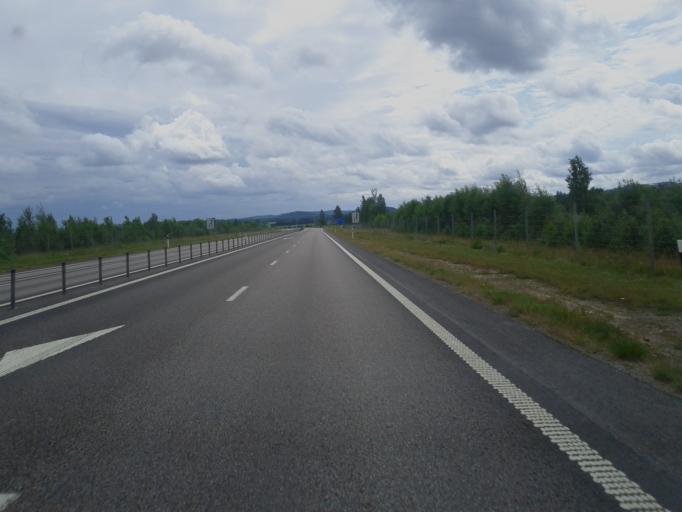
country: SE
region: Dalarna
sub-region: Borlange Kommun
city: Ornas
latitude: 60.4280
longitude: 15.5294
